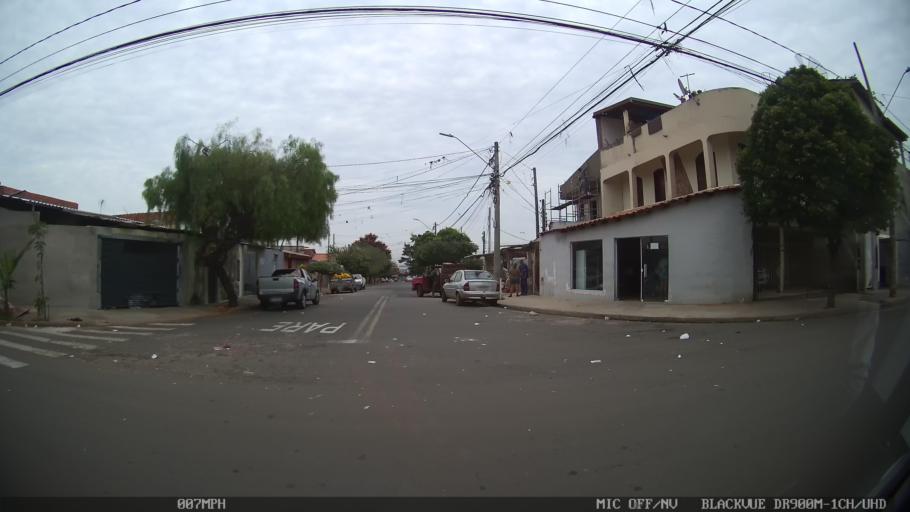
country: BR
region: Sao Paulo
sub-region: Americana
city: Americana
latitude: -22.7624
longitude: -47.3283
